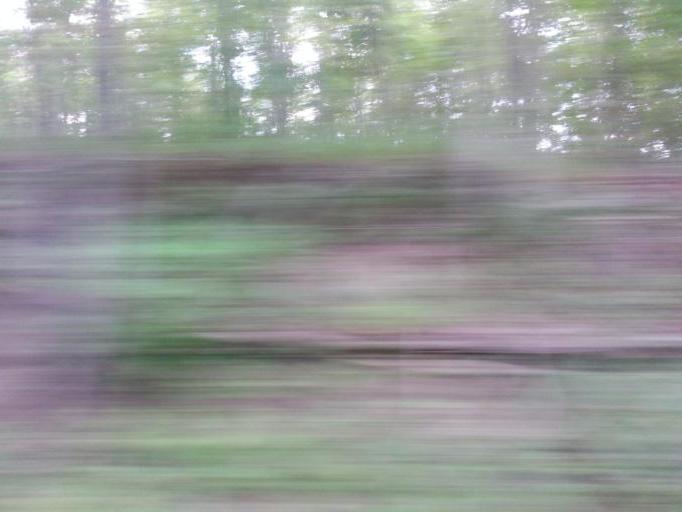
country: US
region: Tennessee
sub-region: Knox County
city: Knoxville
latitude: 35.9030
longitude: -83.8759
